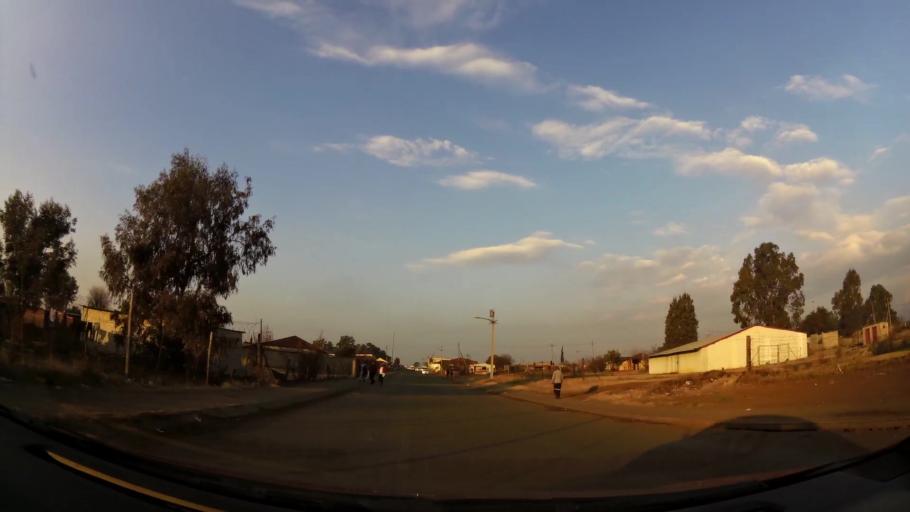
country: ZA
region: Gauteng
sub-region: City of Johannesburg Metropolitan Municipality
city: Orange Farm
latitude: -26.5347
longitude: 27.8468
